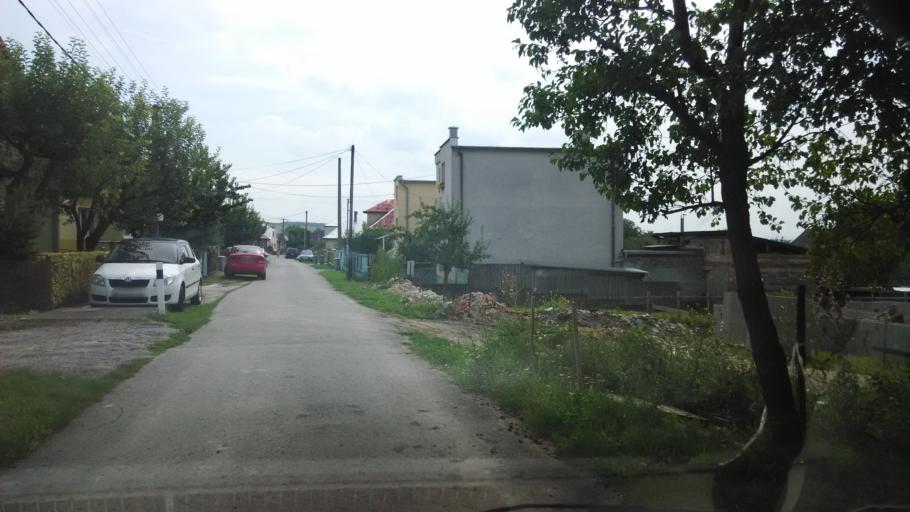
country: SK
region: Nitriansky
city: Trencianske Teplice
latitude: 48.8084
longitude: 18.1906
